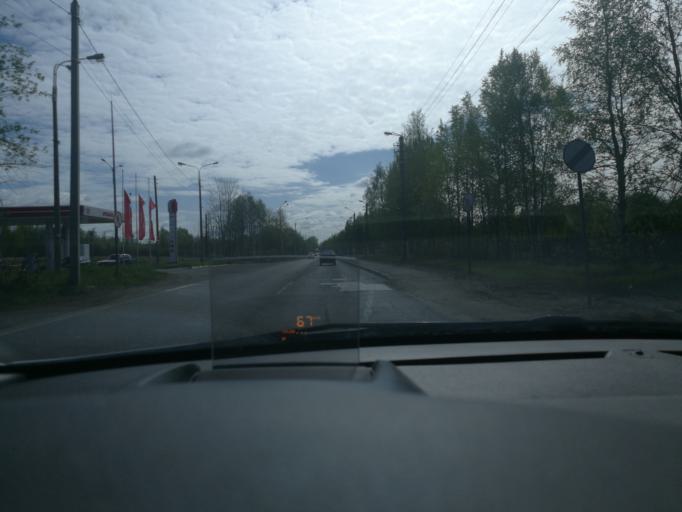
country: RU
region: Arkhangelskaya
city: Arkhangel'sk
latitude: 64.5978
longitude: 40.5594
